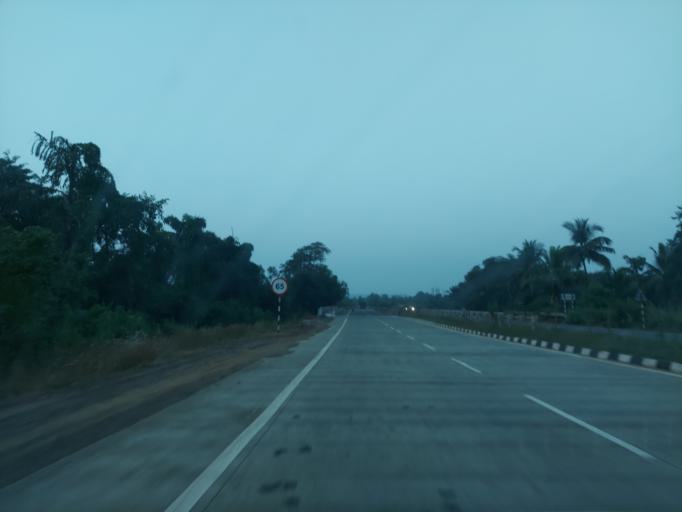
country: IN
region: Maharashtra
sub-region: Sindhudurg
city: Kudal
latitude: 16.0967
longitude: 73.7064
